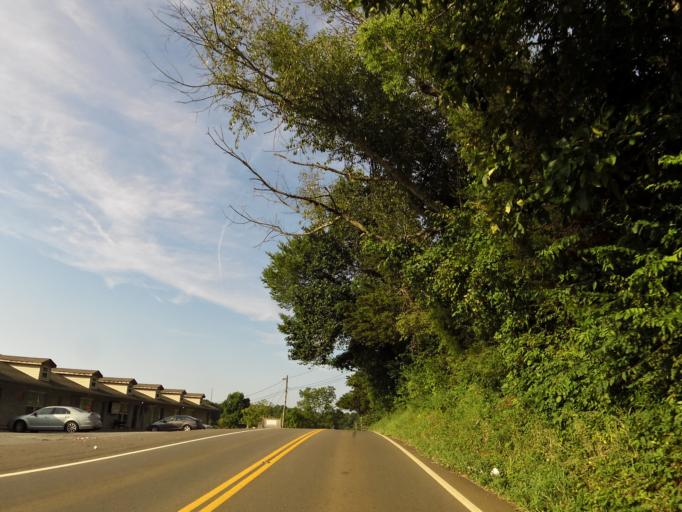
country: US
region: Tennessee
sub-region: Sevier County
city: Seymour
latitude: 35.8588
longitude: -83.7725
